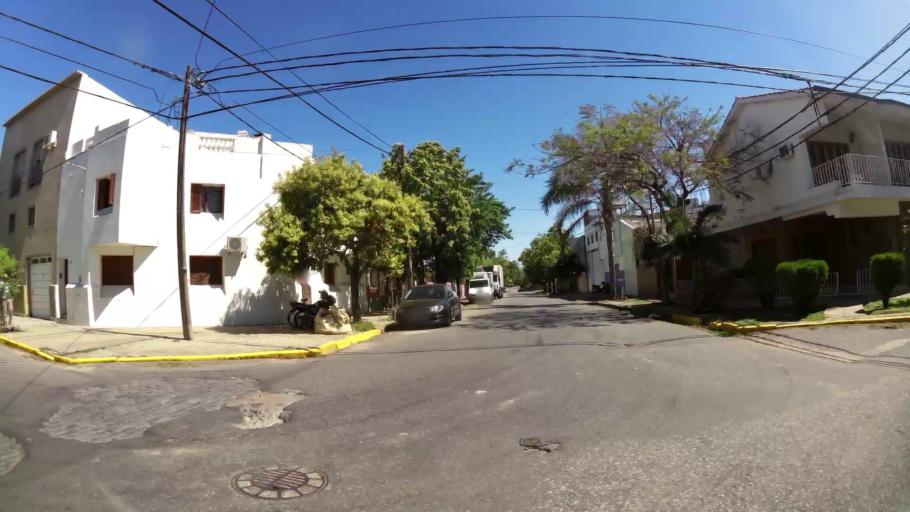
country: AR
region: Santa Fe
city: Santa Fe de la Vera Cruz
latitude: -31.6426
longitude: -60.6937
